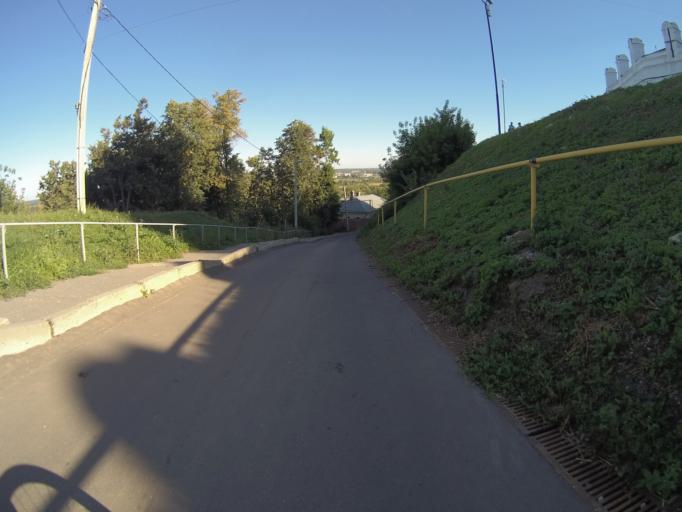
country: RU
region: Vladimir
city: Vladimir
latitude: 56.1277
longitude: 40.4100
